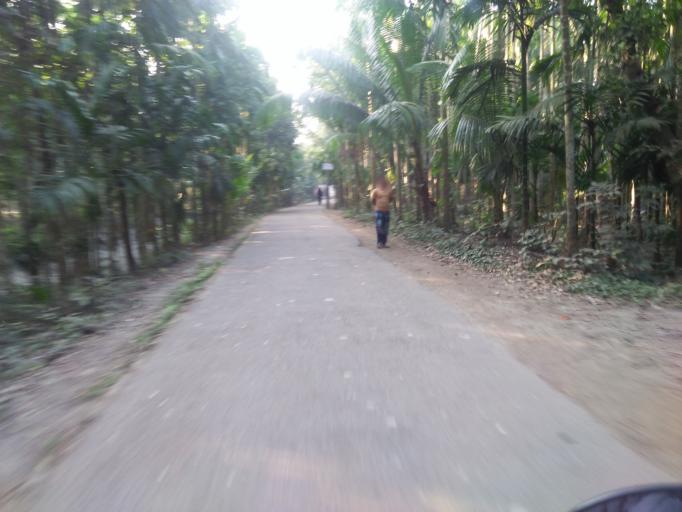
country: BD
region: Barisal
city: Bhola
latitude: 22.7523
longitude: 90.6328
